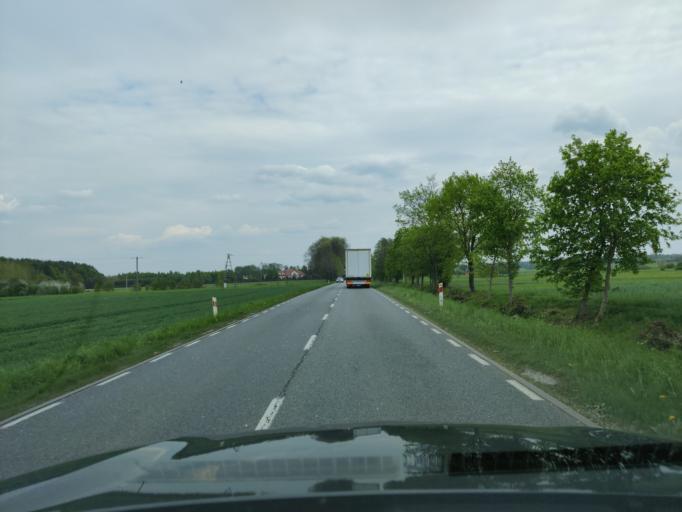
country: PL
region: Masovian Voivodeship
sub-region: Powiat wyszkowski
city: Rzasnik
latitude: 52.6278
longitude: 21.3269
